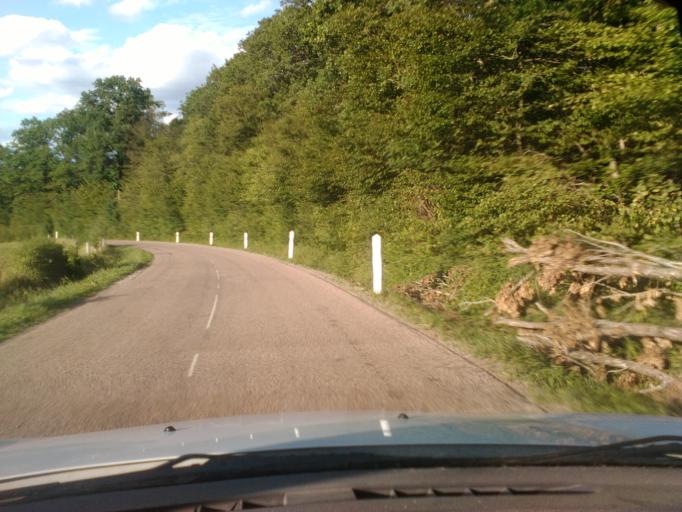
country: FR
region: Lorraine
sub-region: Departement des Vosges
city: Mirecourt
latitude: 48.3466
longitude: 6.0376
